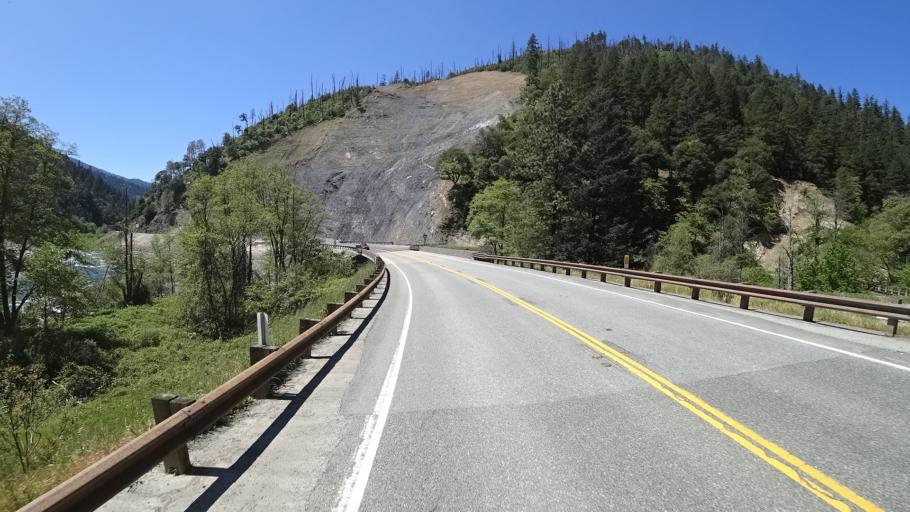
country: US
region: California
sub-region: Trinity County
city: Hayfork
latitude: 40.7799
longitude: -123.3091
